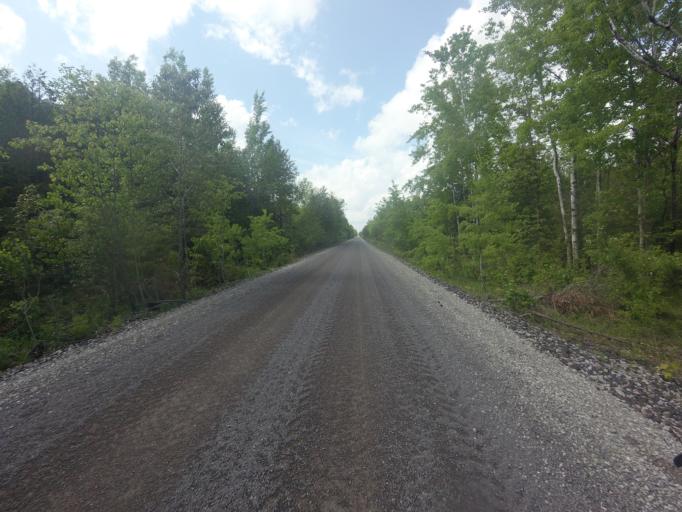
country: CA
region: Ontario
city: Carleton Place
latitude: 45.0500
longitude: -76.0890
